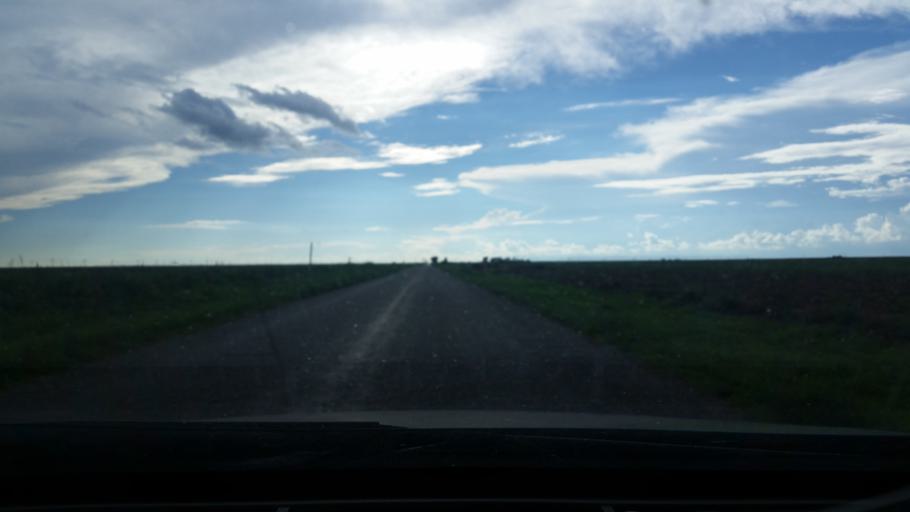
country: US
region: New Mexico
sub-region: Curry County
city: Clovis
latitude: 34.4630
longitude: -103.2168
